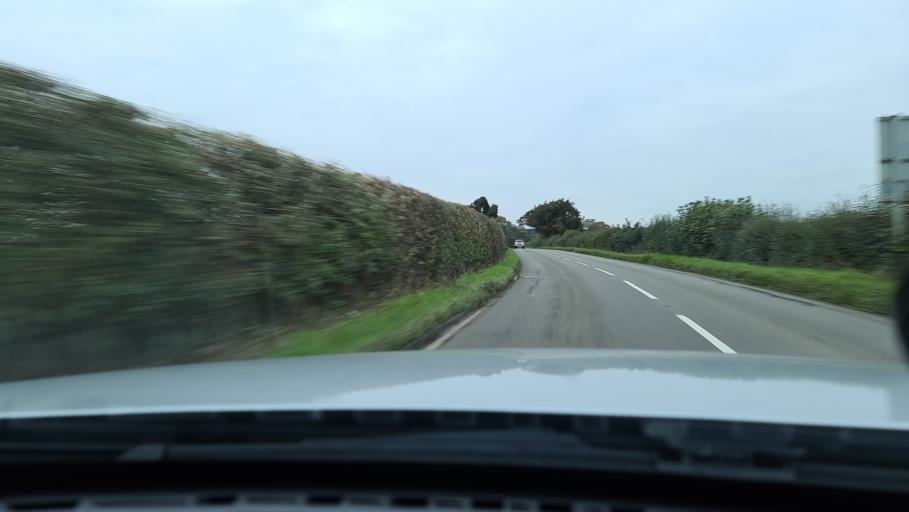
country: GB
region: England
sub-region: Oxfordshire
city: Somerton
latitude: 51.9171
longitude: -1.2386
